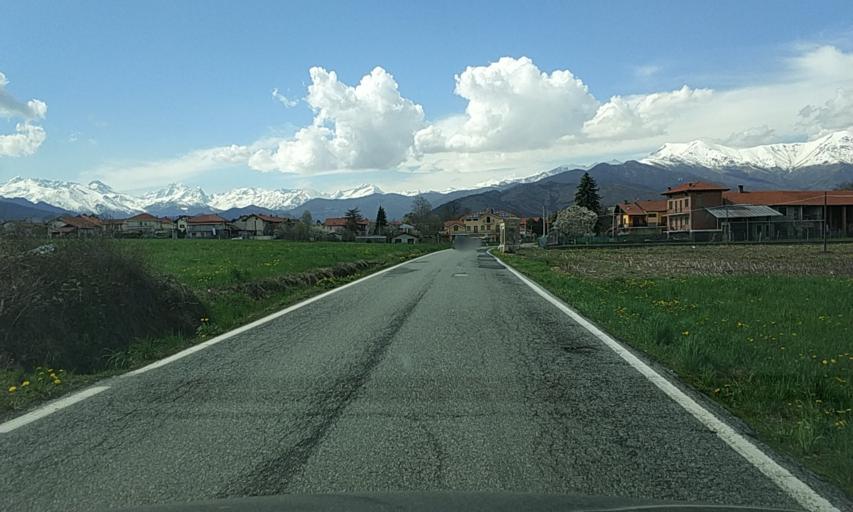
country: IT
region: Piedmont
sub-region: Provincia di Torino
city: Nole
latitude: 45.2553
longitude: 7.5858
